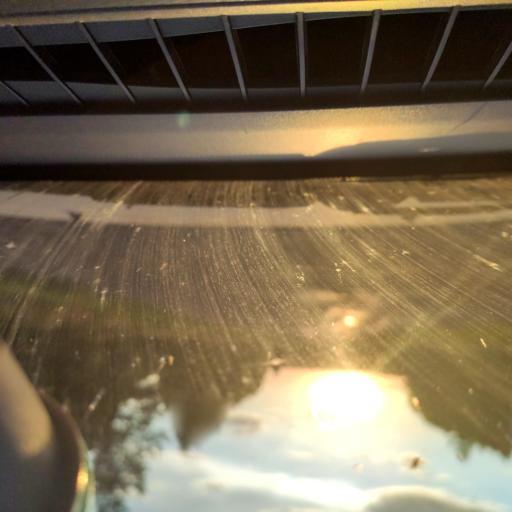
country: RU
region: Kirov
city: Kotel'nich
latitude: 58.5596
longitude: 48.1945
